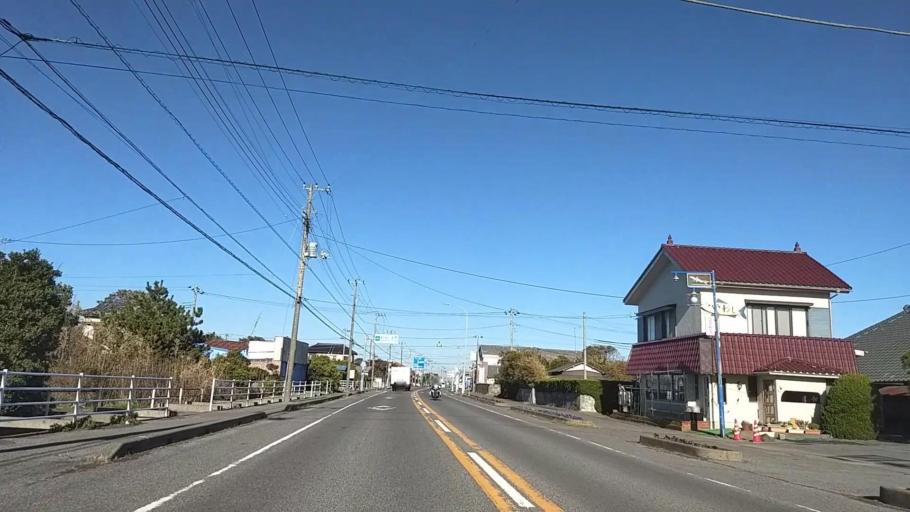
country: JP
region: Chiba
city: Togane
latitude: 35.5063
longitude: 140.4322
